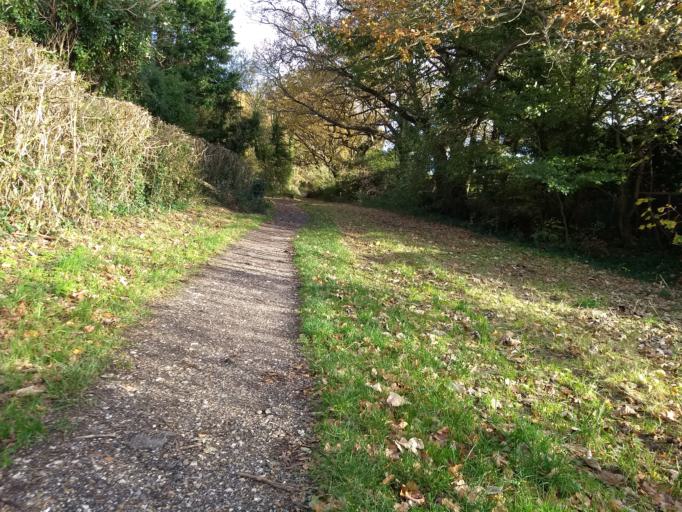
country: GB
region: England
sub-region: Isle of Wight
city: Totland
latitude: 50.6881
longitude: -1.5262
